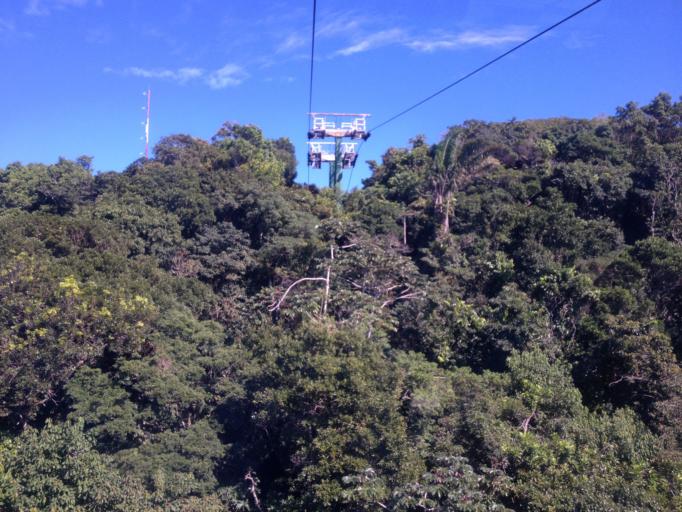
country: BR
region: Santa Catarina
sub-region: Balneario Camboriu
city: Balneario Camboriu
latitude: -27.0004
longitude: -48.5966
